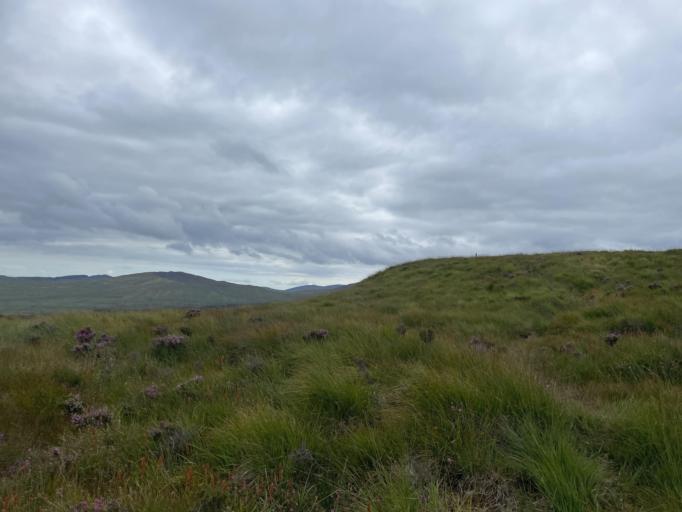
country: GB
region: Scotland
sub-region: Dumfries and Galloway
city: Newton Stewart
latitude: 54.9503
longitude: -4.2837
